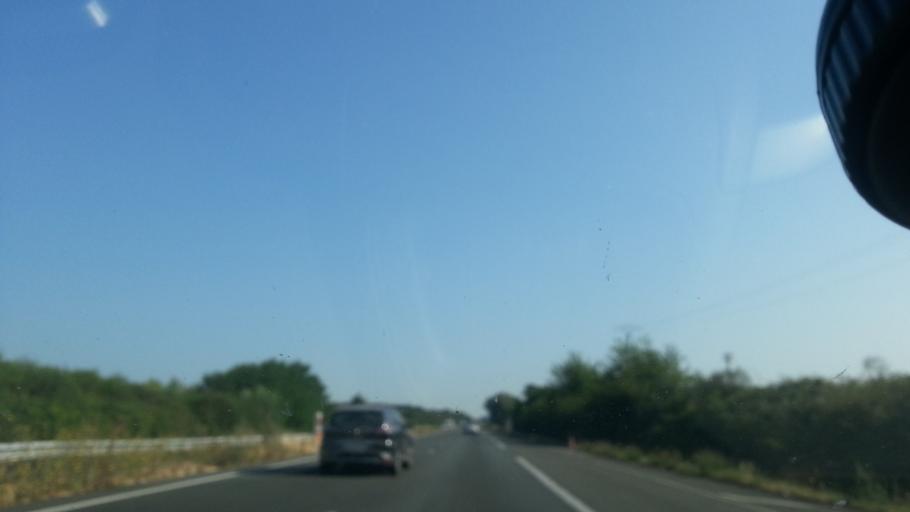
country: FR
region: Poitou-Charentes
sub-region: Departement de la Vienne
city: Antran
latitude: 46.8962
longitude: 0.5201
